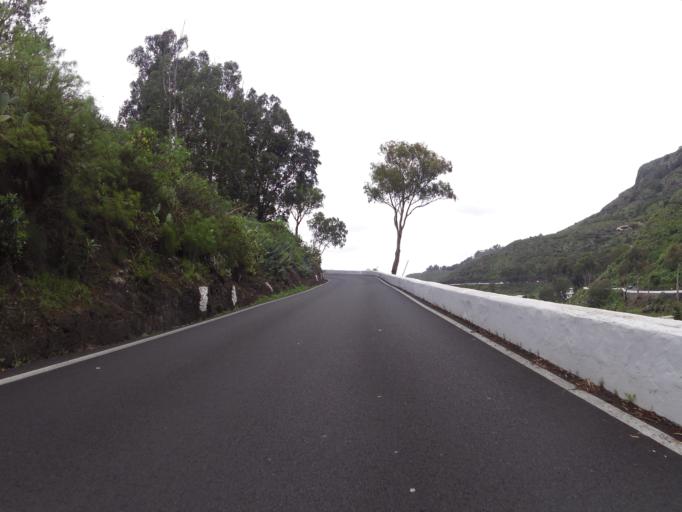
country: ES
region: Canary Islands
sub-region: Provincia de Las Palmas
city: Teror
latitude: 28.0777
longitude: -15.5185
